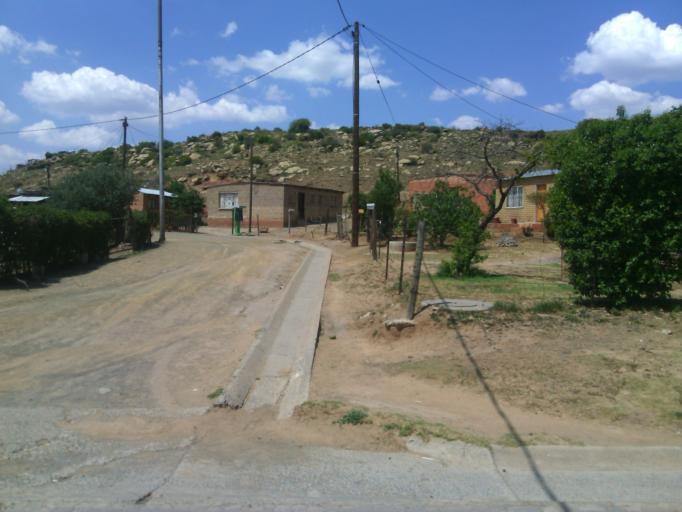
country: ZA
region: Orange Free State
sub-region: Xhariep District Municipality
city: Dewetsdorp
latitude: -29.5826
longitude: 26.6796
